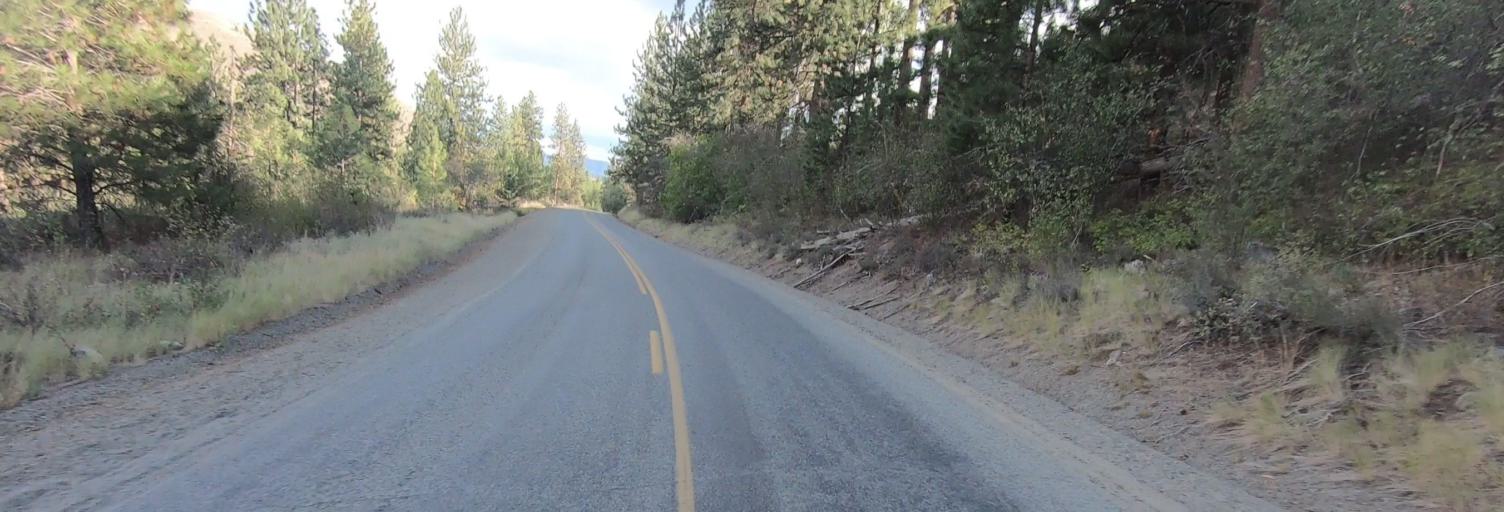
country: US
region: Washington
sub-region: Okanogan County
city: Brewster
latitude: 48.5412
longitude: -120.1931
